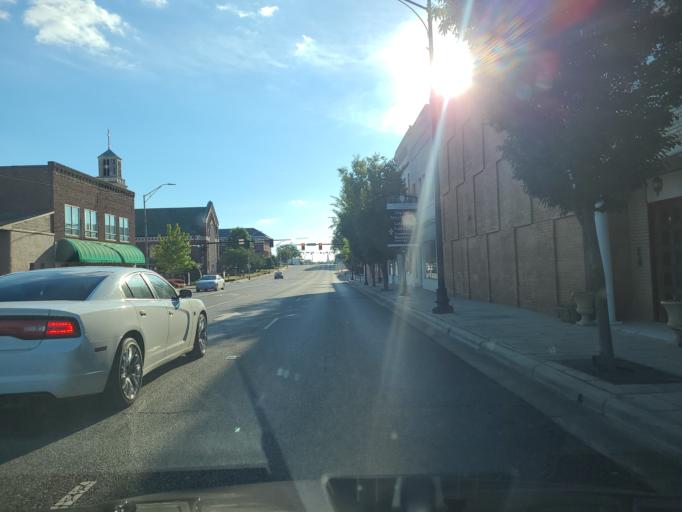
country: US
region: North Carolina
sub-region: Gaston County
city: Gastonia
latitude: 35.2623
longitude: -81.1828
